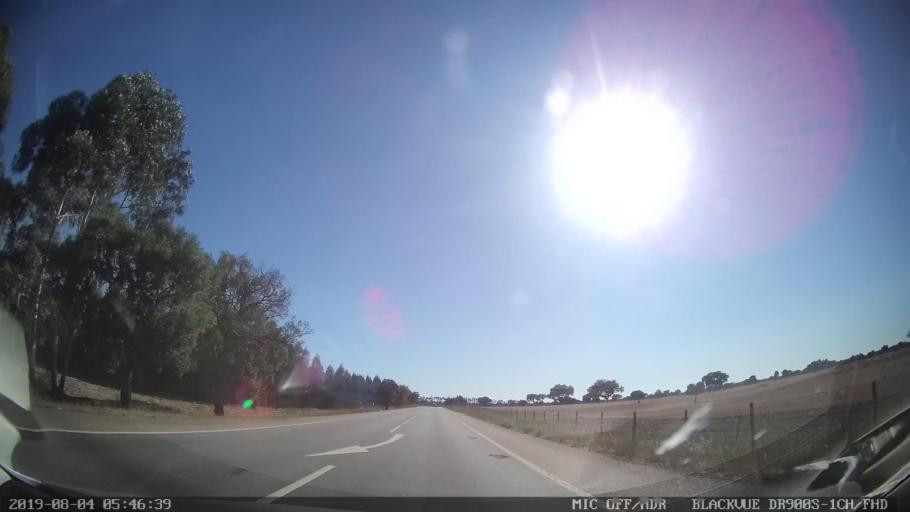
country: PT
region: Portalegre
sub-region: Gaviao
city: Gaviao
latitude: 39.4480
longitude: -7.7915
